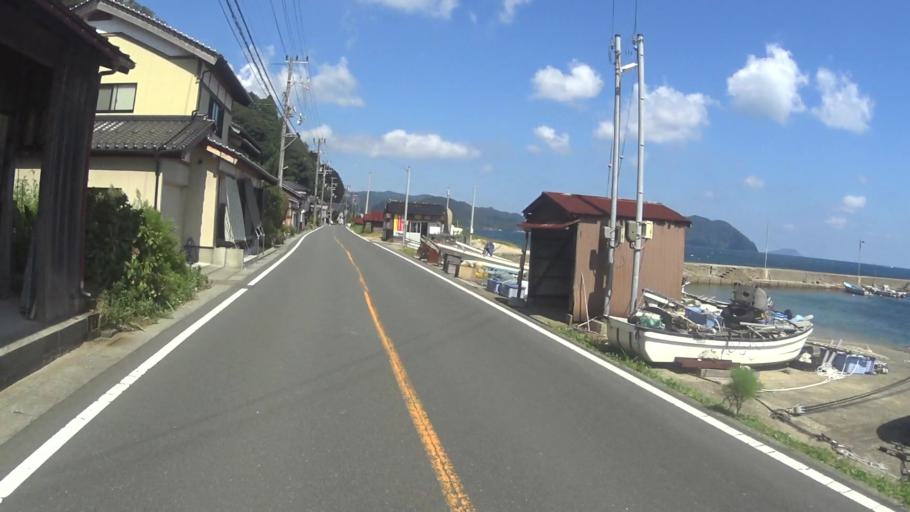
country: JP
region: Kyoto
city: Miyazu
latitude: 35.6495
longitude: 135.2532
